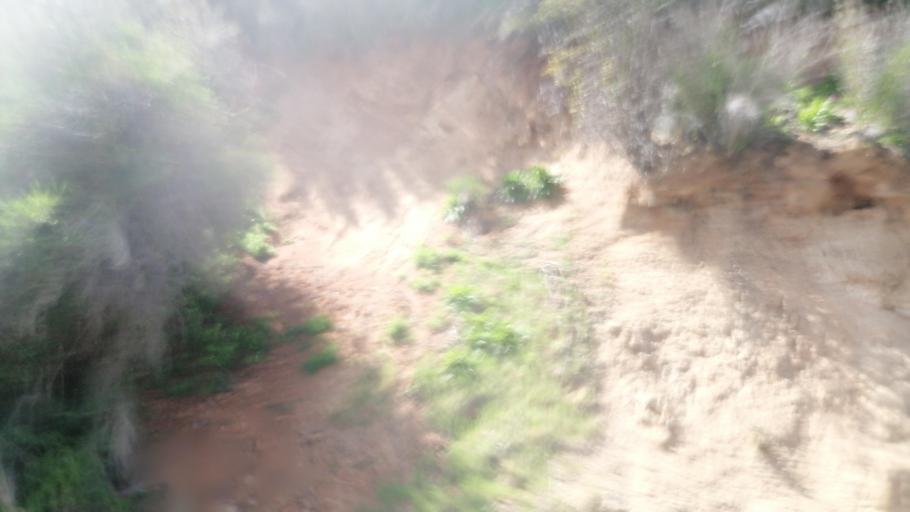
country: CL
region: Valparaiso
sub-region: Provincia de Marga Marga
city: Limache
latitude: -33.1804
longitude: -71.1799
